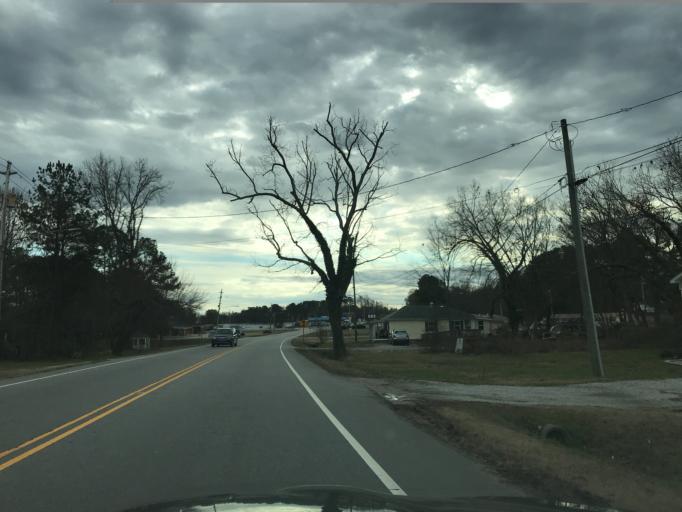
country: US
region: North Carolina
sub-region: Franklin County
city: Louisburg
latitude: 36.1091
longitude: -78.2917
